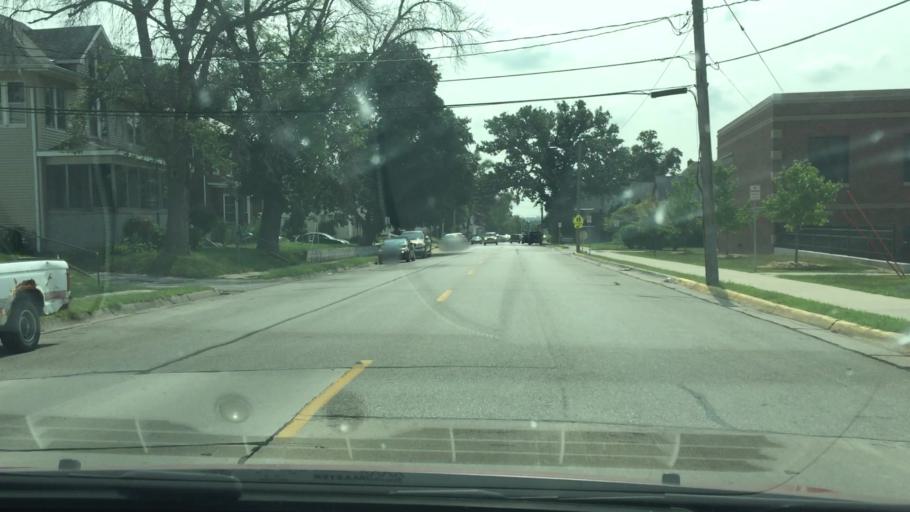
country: US
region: Iowa
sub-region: Muscatine County
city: Muscatine
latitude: 41.4297
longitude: -91.0476
